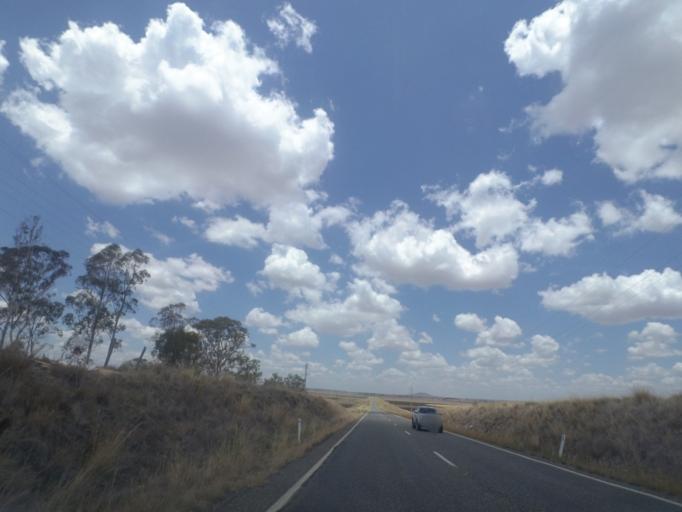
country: AU
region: Queensland
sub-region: Toowoomba
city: Top Camp
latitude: -27.8927
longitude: 151.9737
